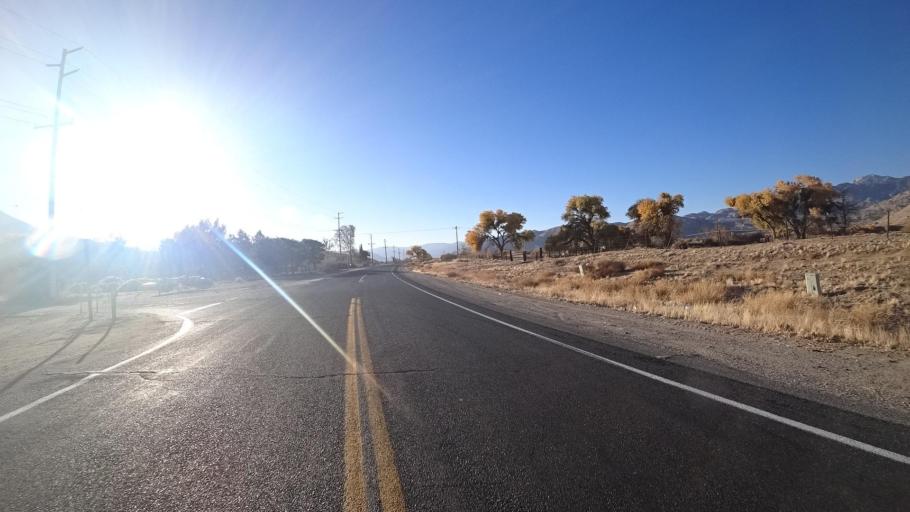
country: US
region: California
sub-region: Kern County
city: Weldon
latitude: 35.6672
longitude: -118.2676
